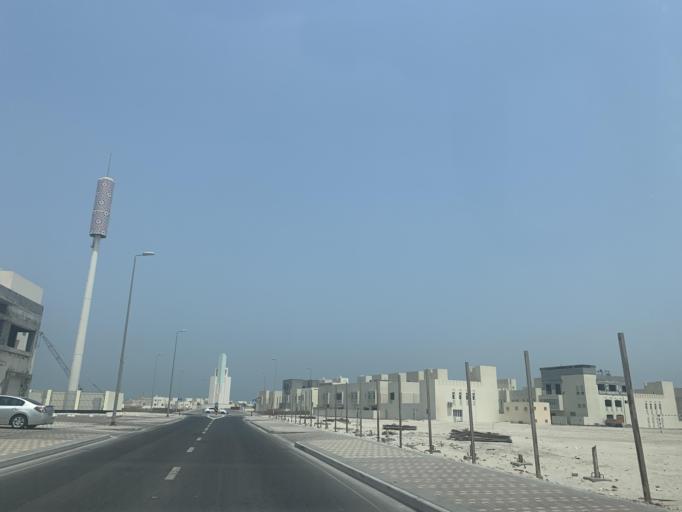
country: BH
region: Muharraq
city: Al Hadd
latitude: 26.2328
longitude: 50.6625
